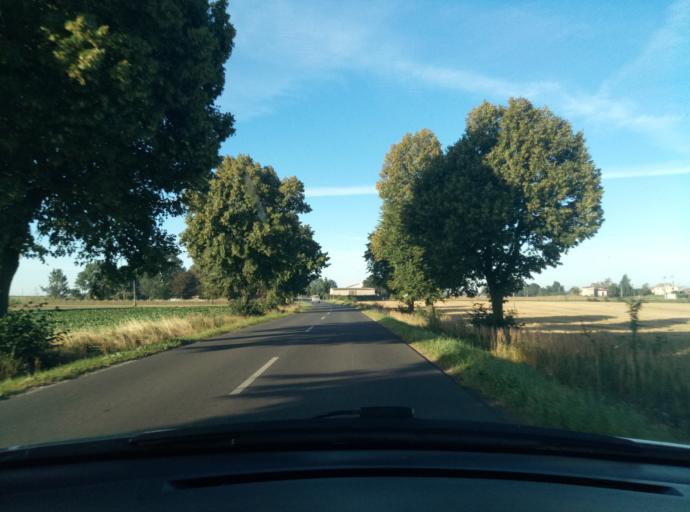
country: PL
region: Kujawsko-Pomorskie
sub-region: Powiat golubsko-dobrzynski
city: Kowalewo Pomorskie
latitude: 53.2057
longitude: 18.9201
